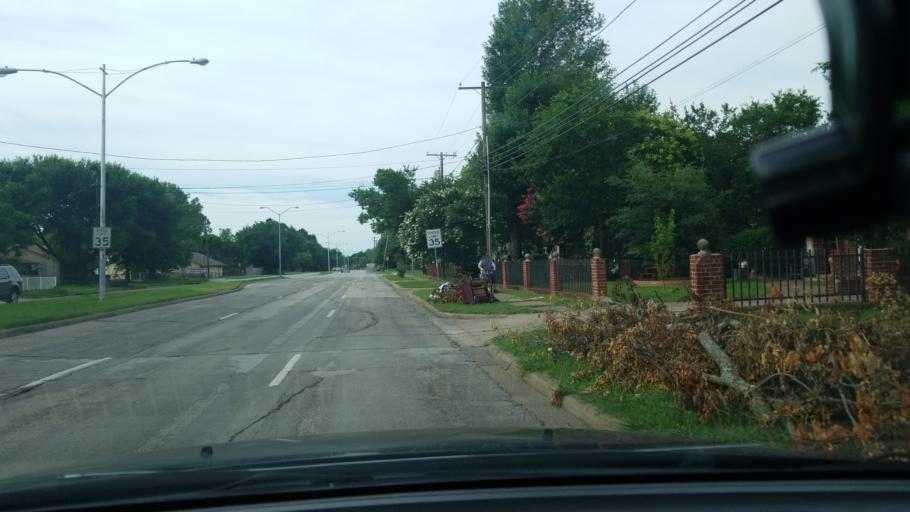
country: US
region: Texas
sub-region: Dallas County
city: Balch Springs
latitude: 32.7603
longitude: -96.6656
